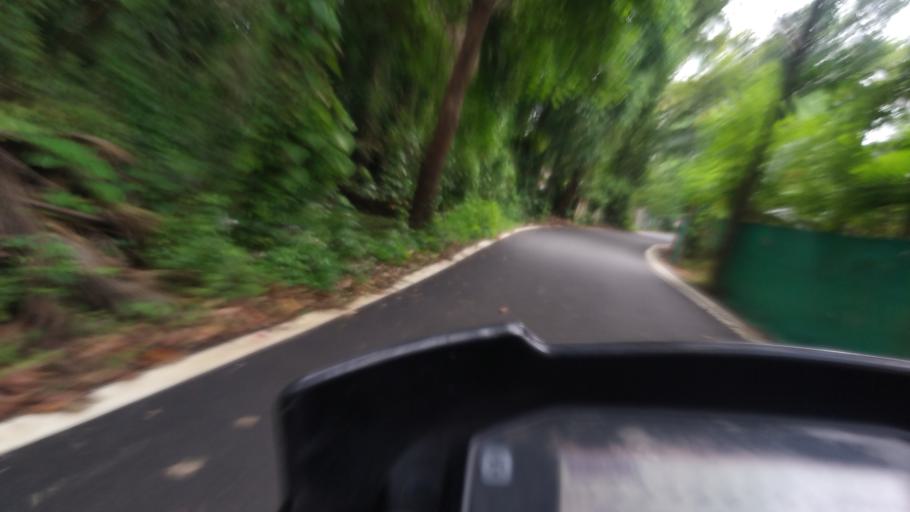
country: IN
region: Kerala
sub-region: Ernakulam
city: Elur
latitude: 10.0589
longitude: 76.2262
